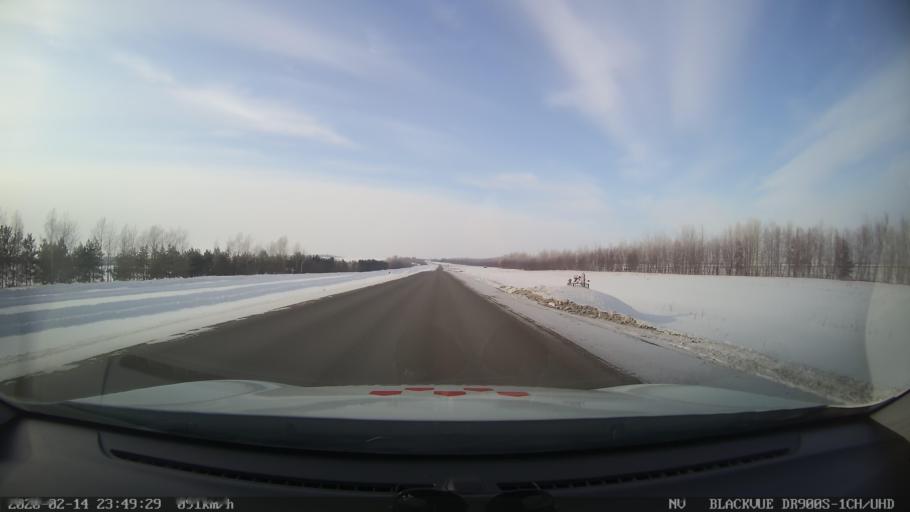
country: RU
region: Tatarstan
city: Kuybyshevskiy Zaton
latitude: 55.2540
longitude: 49.1809
